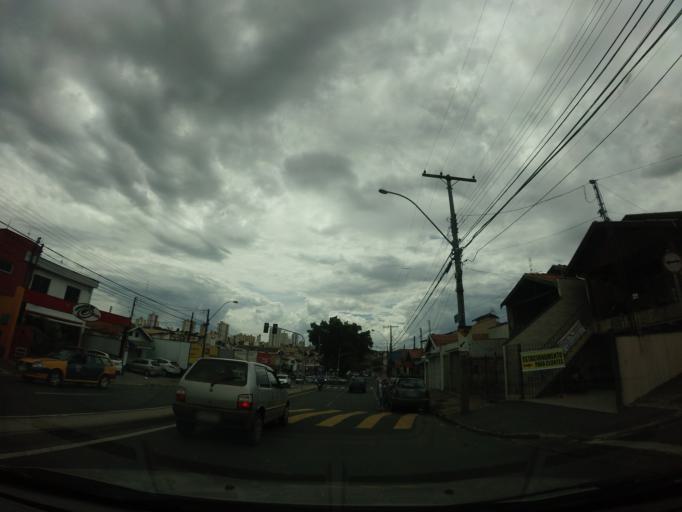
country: BR
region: Sao Paulo
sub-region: Piracicaba
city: Piracicaba
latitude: -22.7413
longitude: -47.6272
